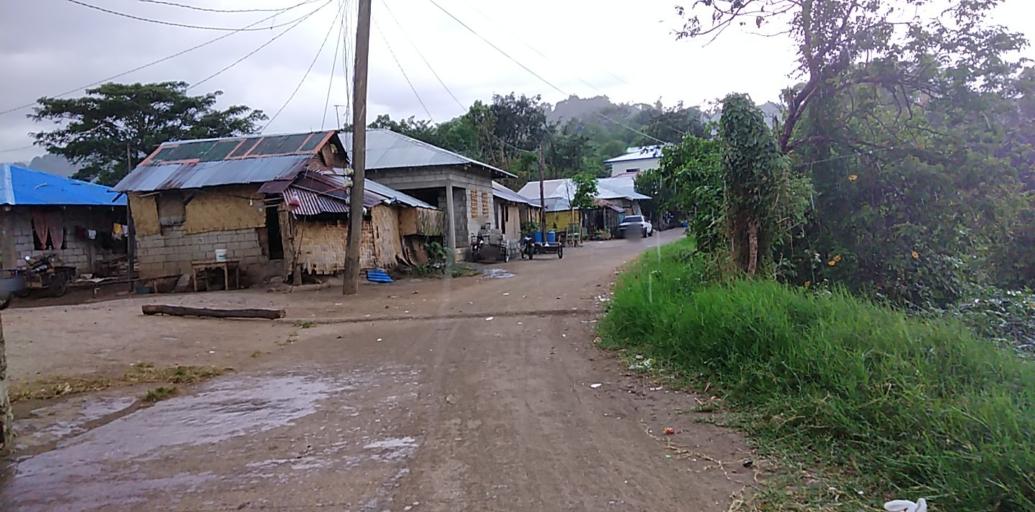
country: PH
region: Central Luzon
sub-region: Province of Pampanga
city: Babo-Pangulo
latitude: 15.1084
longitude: 120.4889
